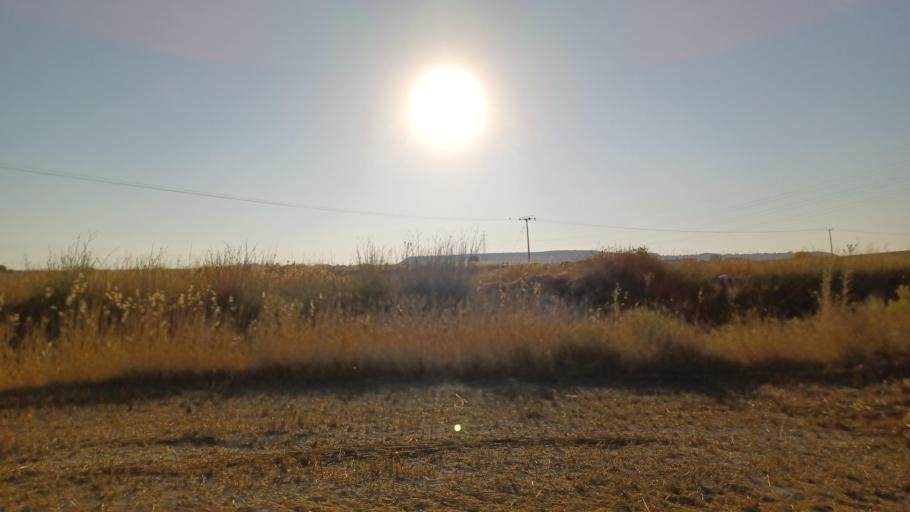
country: CY
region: Larnaka
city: Voroklini
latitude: 34.9885
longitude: 33.6744
